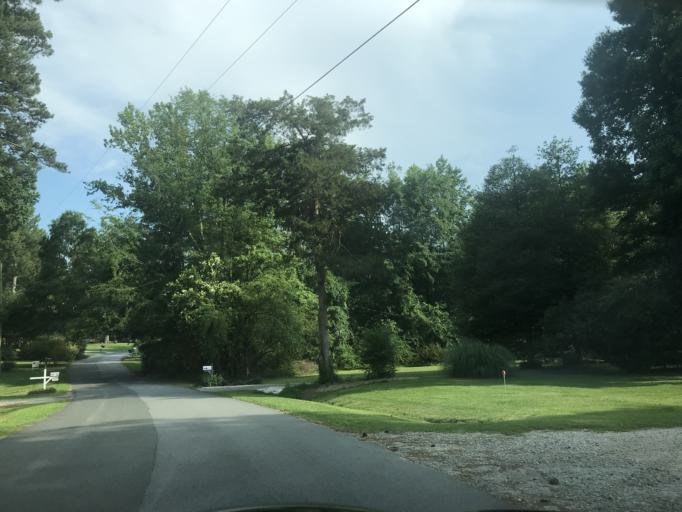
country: US
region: North Carolina
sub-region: Wake County
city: Raleigh
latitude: 35.8198
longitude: -78.5722
